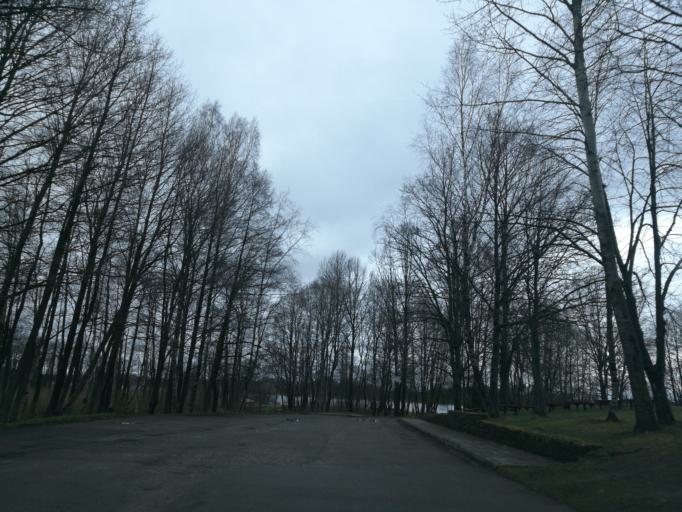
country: LT
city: Rietavas
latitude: 55.7014
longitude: 21.7341
